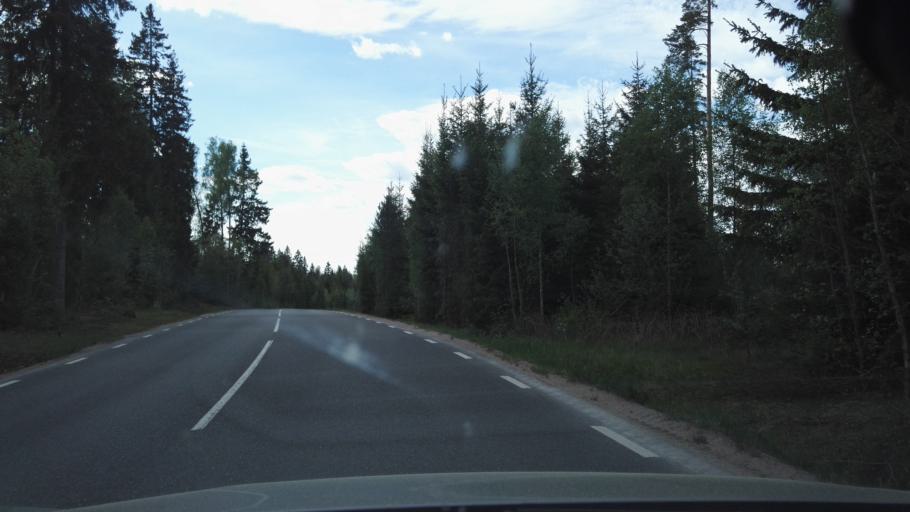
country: SE
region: Kronoberg
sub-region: Vaxjo Kommun
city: Braas
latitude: 57.1859
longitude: 14.9632
